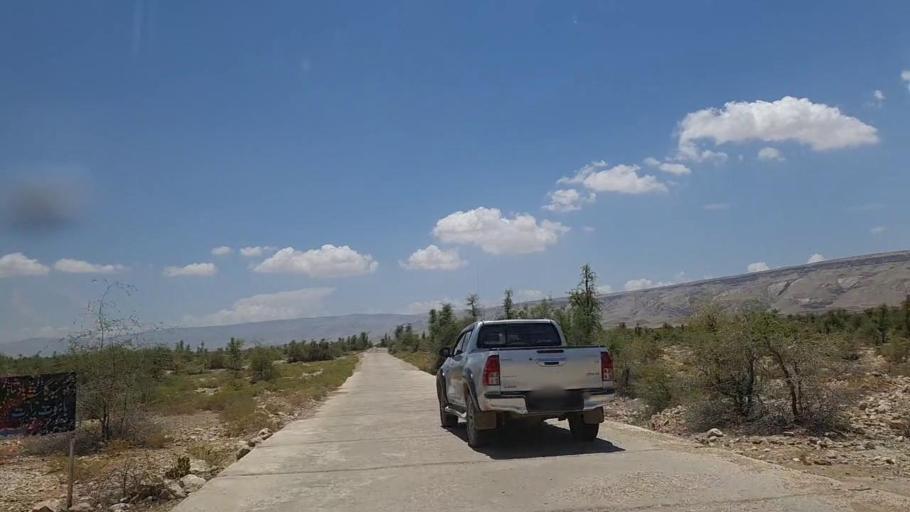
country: PK
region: Sindh
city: Bhan
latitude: 26.2830
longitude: 67.5310
